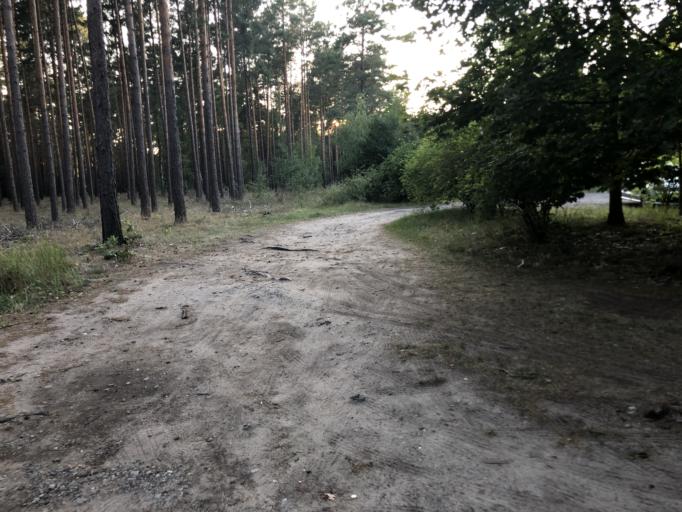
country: DE
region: Brandenburg
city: Gross Lindow
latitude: 52.2514
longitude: 14.4781
